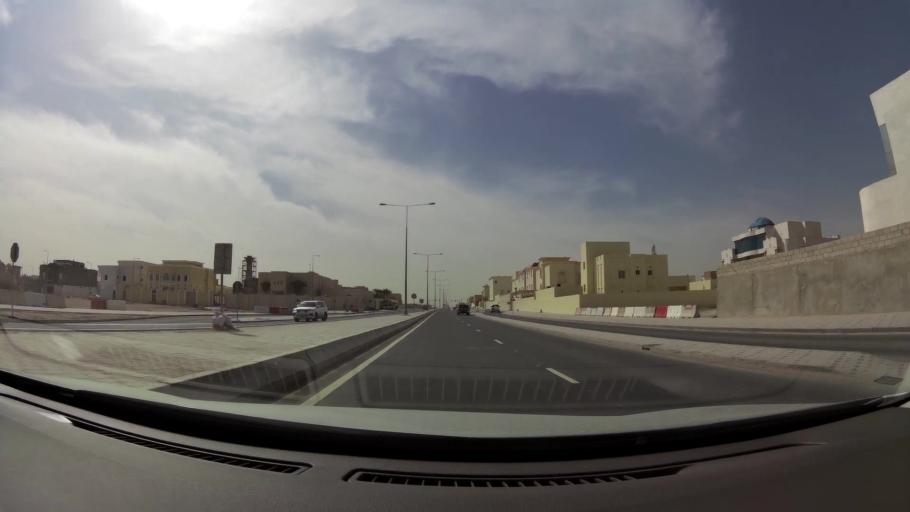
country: QA
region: Baladiyat ar Rayyan
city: Ar Rayyan
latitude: 25.3234
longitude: 51.3926
